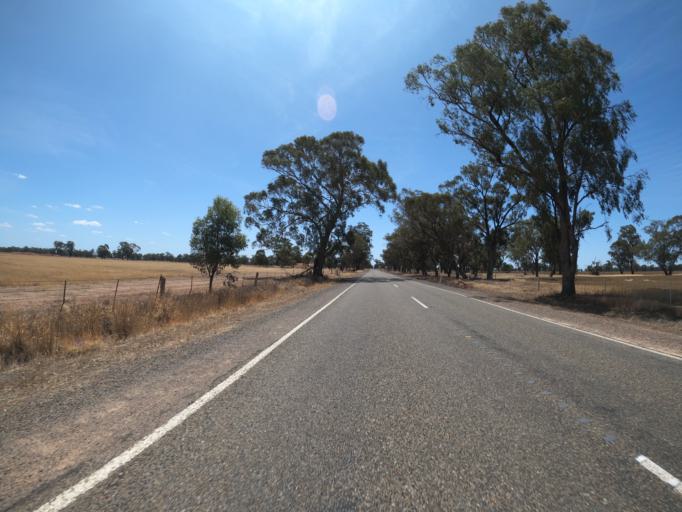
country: AU
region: Victoria
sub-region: Moira
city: Yarrawonga
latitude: -36.1848
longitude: 145.9672
